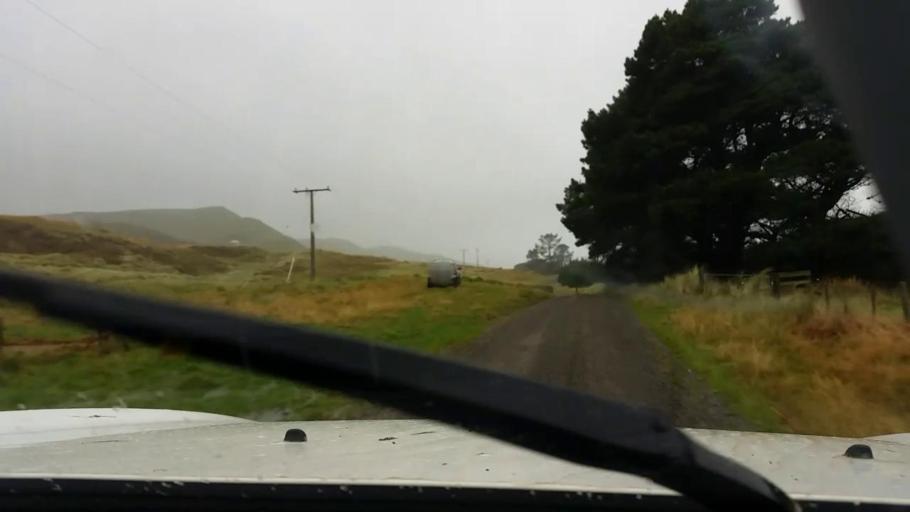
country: NZ
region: Wellington
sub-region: Masterton District
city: Masterton
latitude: -41.2534
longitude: 175.9120
